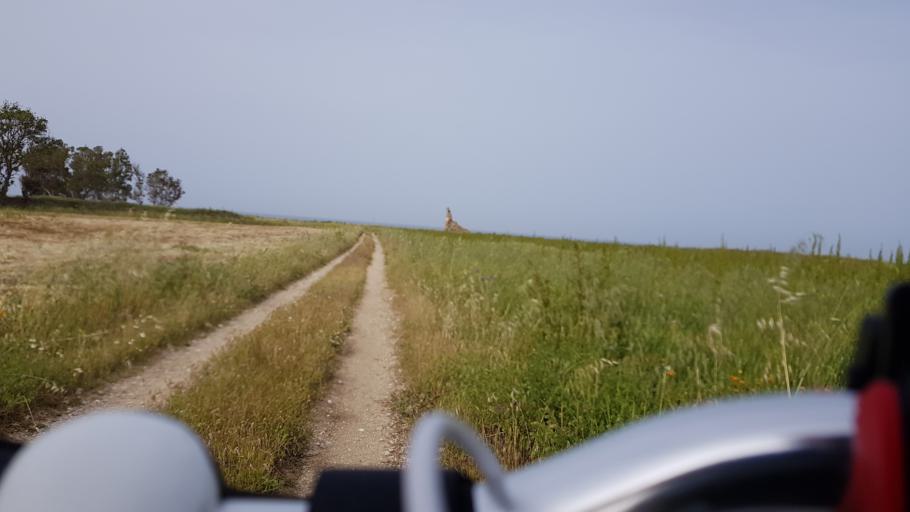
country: IT
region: Apulia
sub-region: Provincia di Brindisi
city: La Rosa
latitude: 40.5808
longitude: 18.0393
